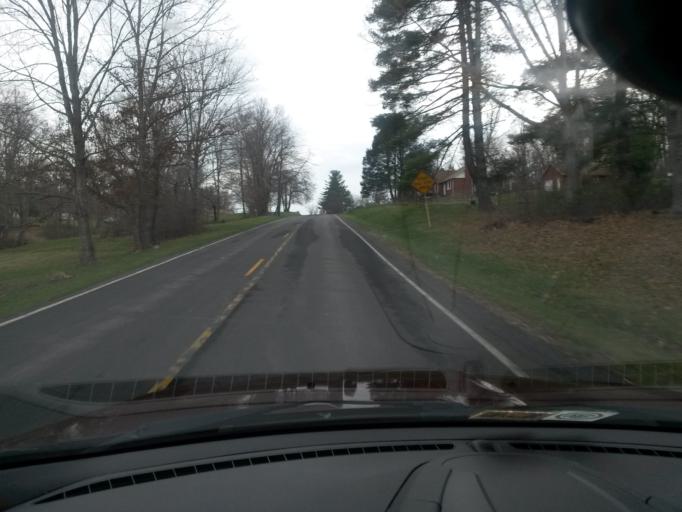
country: US
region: Virginia
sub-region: Bath County
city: Warm Springs
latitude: 38.0970
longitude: -79.7772
